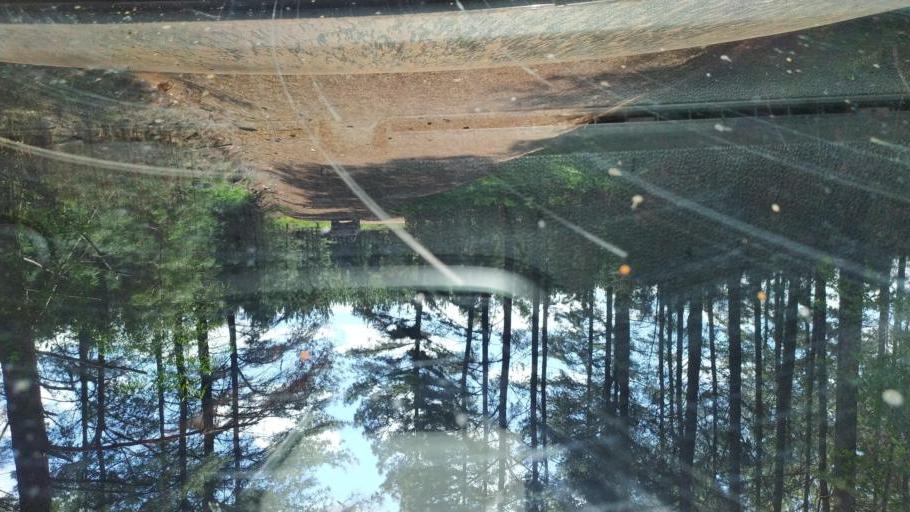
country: AR
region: Corrientes
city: Santo Tome
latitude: -28.4603
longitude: -55.9964
